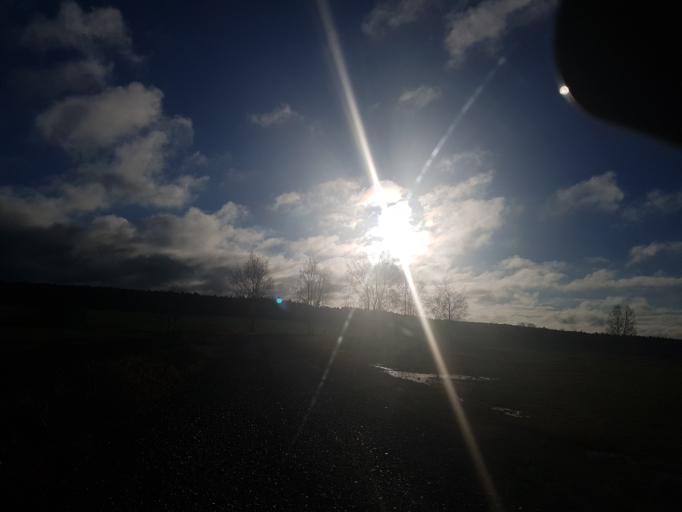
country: DE
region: Brandenburg
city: Schonborn
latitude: 51.5484
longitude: 13.4714
